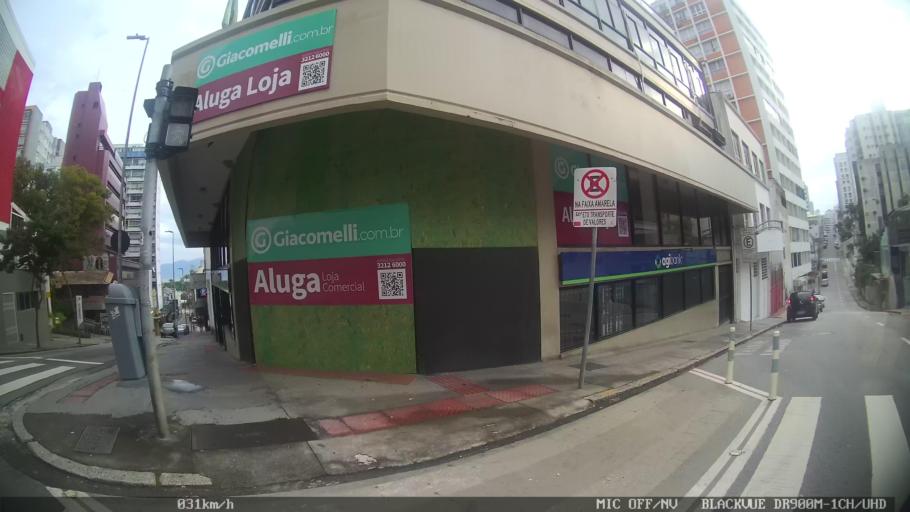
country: BR
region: Santa Catarina
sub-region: Florianopolis
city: Florianopolis
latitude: -27.5948
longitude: -48.5531
